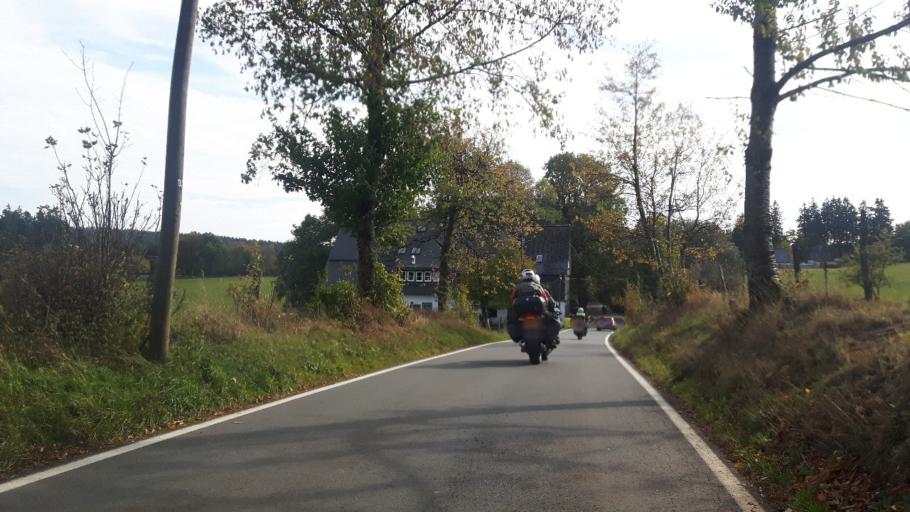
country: DE
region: North Rhine-Westphalia
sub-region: Regierungsbezirk Arnsberg
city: Erndtebruck
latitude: 50.8933
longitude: 8.2409
